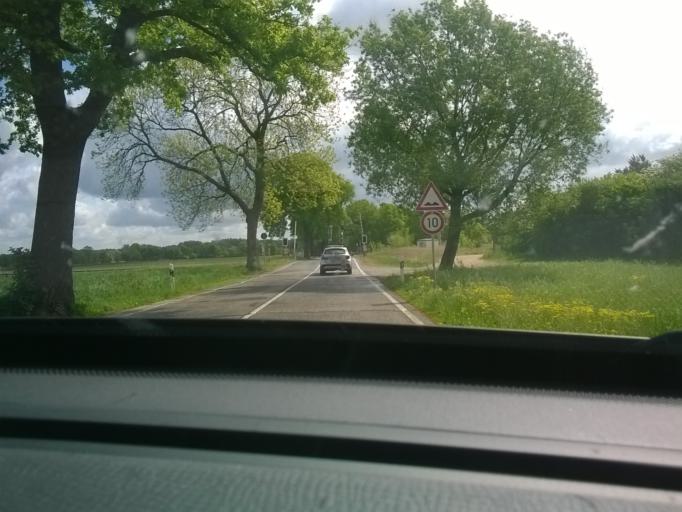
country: DE
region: Brandenburg
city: Wittstock
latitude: 53.0699
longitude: 12.5382
